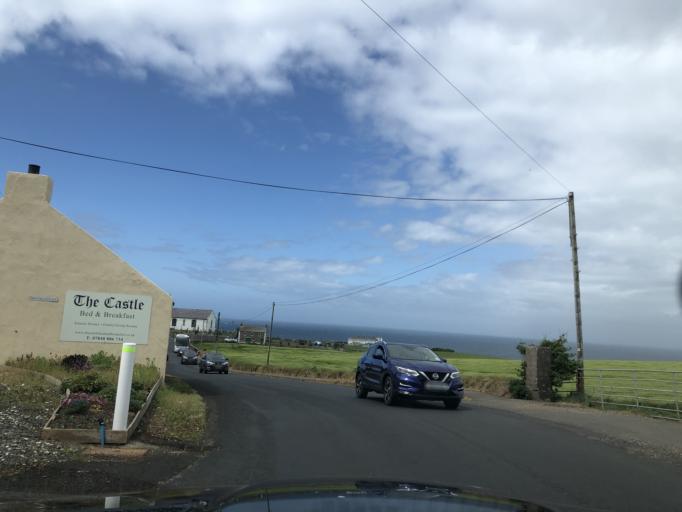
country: GB
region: Northern Ireland
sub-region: Moyle District
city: Ballycastle
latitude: 55.2383
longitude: -6.3655
